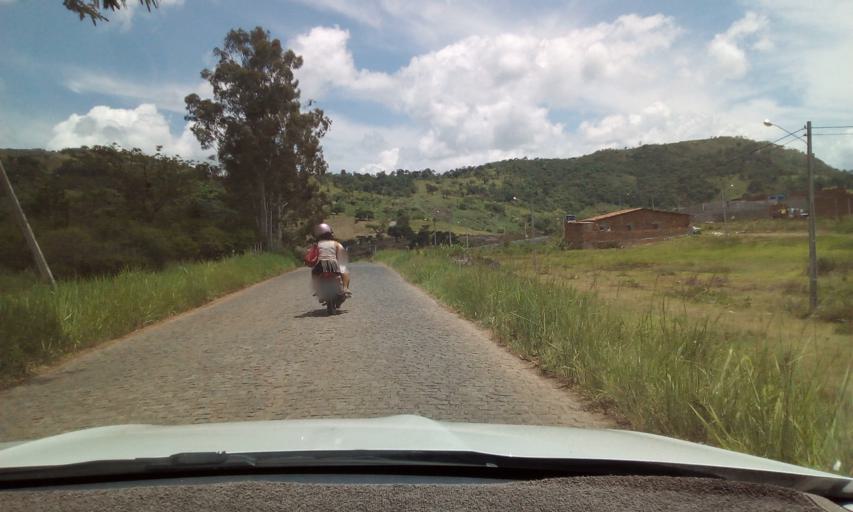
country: BR
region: Pernambuco
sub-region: Bonito
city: Bonito
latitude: -8.4827
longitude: -35.7301
